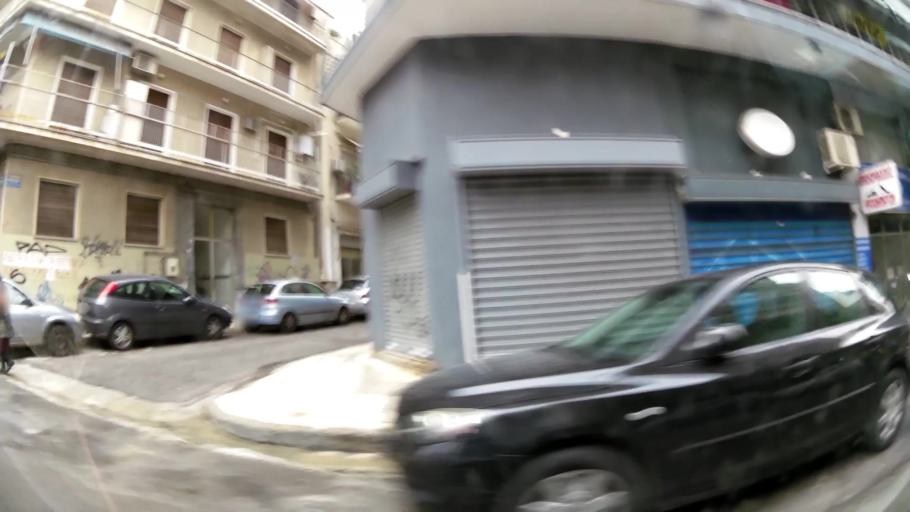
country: GR
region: Attica
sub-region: Nomarchia Athinas
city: Vyronas
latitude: 37.9672
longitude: 23.7515
